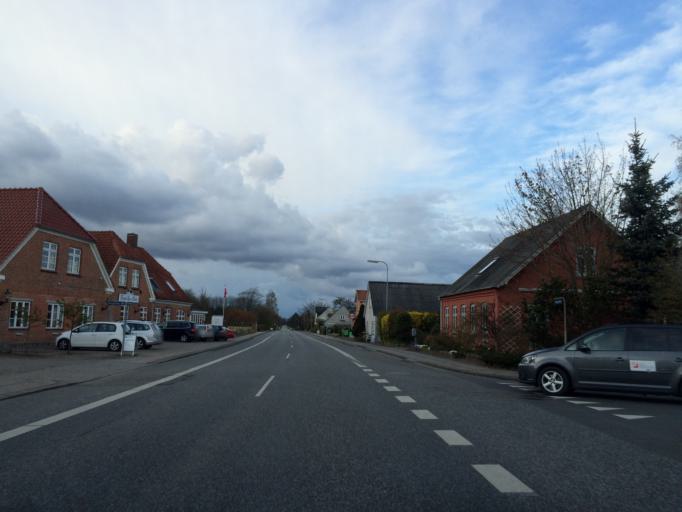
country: DK
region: South Denmark
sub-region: Odense Kommune
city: Bellinge
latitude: 55.3162
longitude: 10.3158
